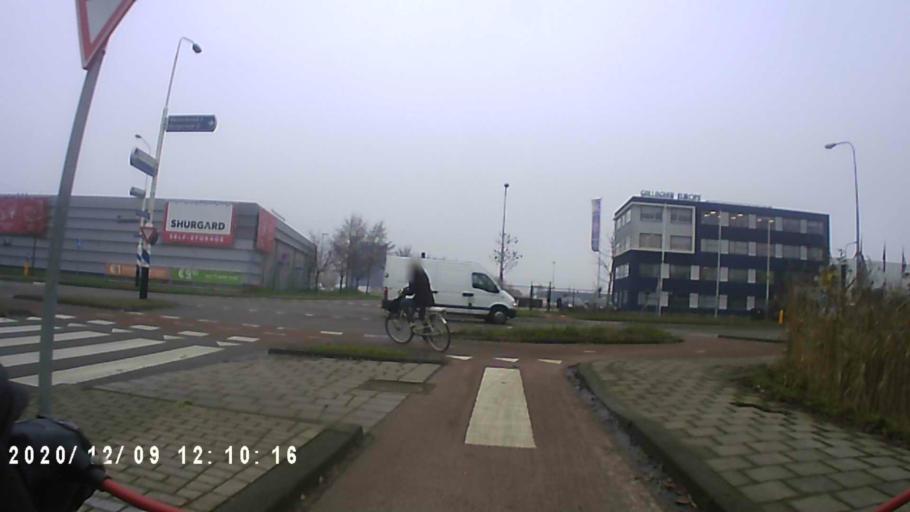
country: NL
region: Groningen
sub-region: Gemeente Groningen
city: Oosterpark
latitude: 53.2035
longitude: 6.6022
